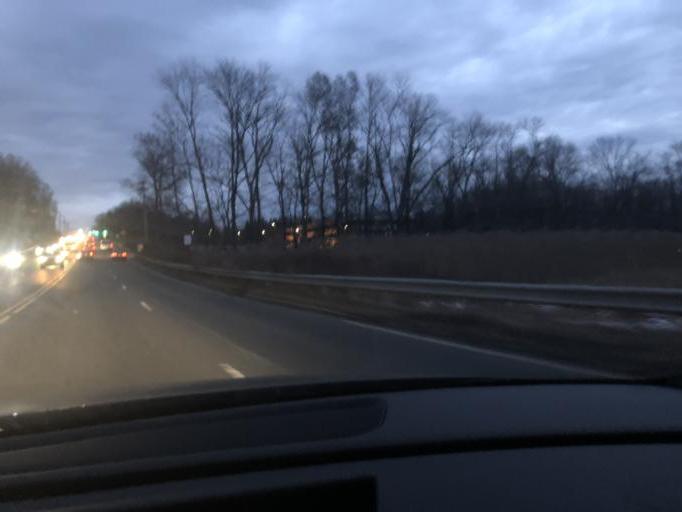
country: US
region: New Jersey
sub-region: Morris County
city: Florham Park
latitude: 40.7906
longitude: -74.4126
